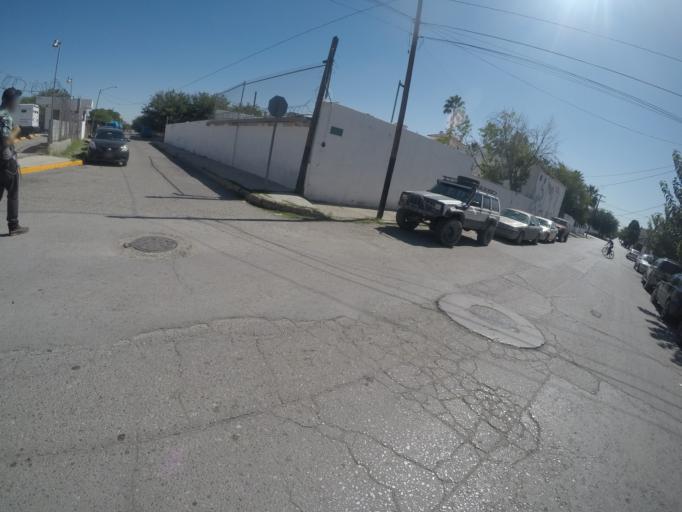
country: MX
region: Chihuahua
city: Ciudad Juarez
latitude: 31.7393
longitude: -106.4711
